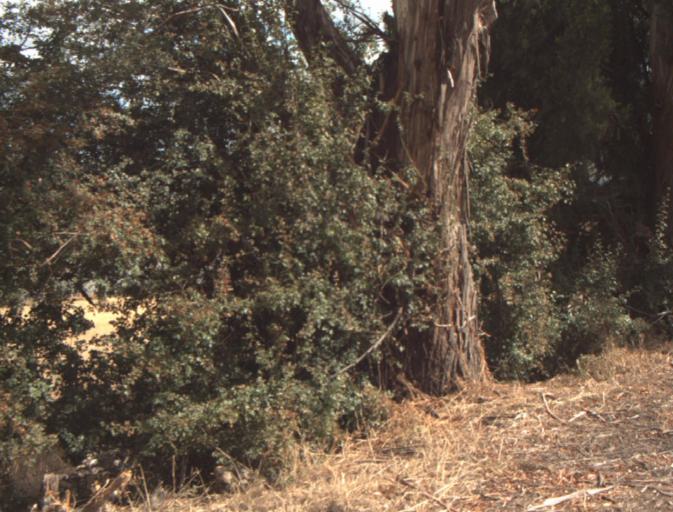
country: AU
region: Tasmania
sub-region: Launceston
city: Mayfield
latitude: -41.3132
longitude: 147.0439
